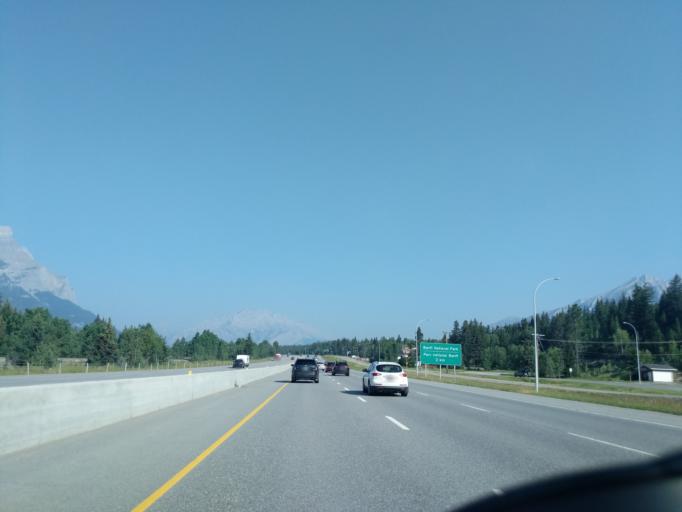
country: CA
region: Alberta
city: Canmore
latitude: 51.1209
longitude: -115.3819
